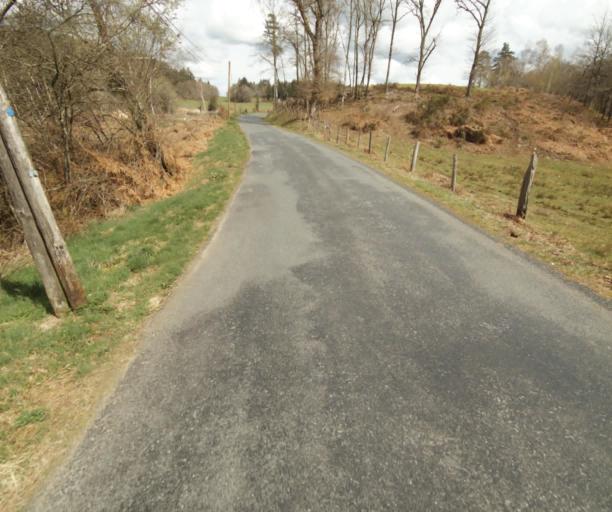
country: FR
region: Limousin
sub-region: Departement de la Correze
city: Correze
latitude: 45.3690
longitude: 1.9309
